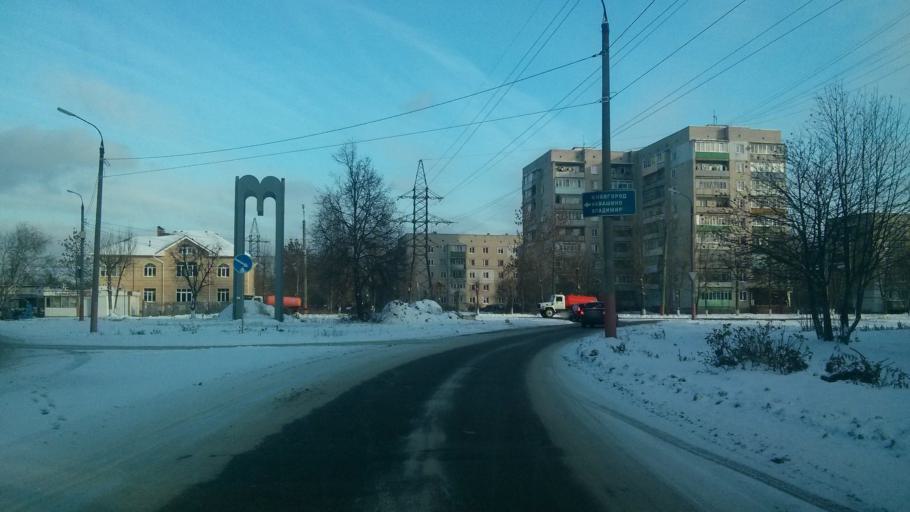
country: RU
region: Vladimir
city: Murom
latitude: 55.5529
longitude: 42.0609
